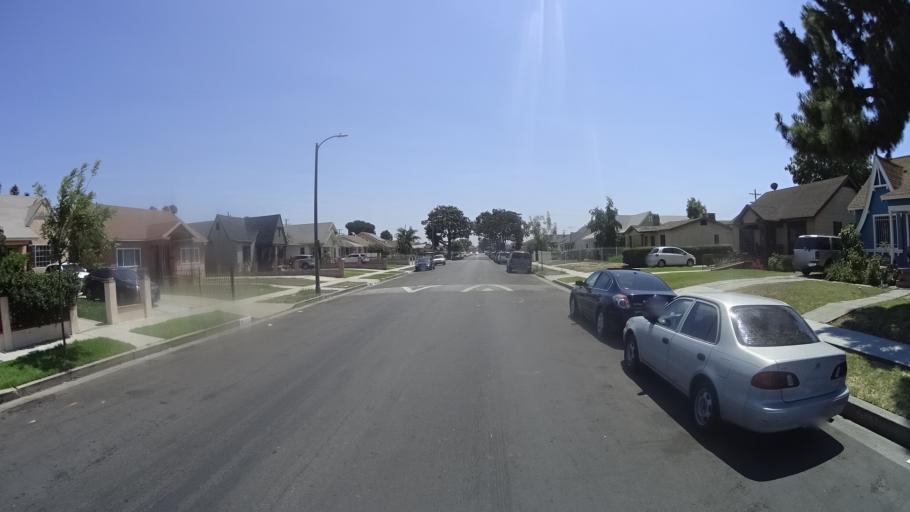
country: US
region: California
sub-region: Los Angeles County
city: Westmont
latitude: 33.9727
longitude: -118.2952
